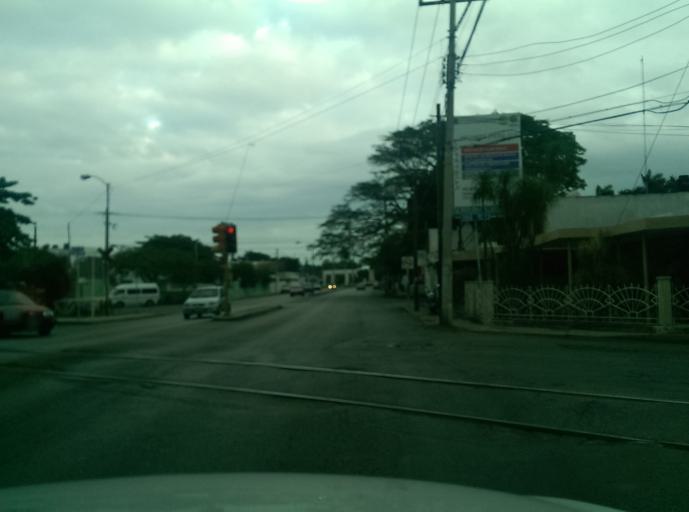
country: MX
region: Yucatan
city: Merida
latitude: 20.9890
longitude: -89.6411
